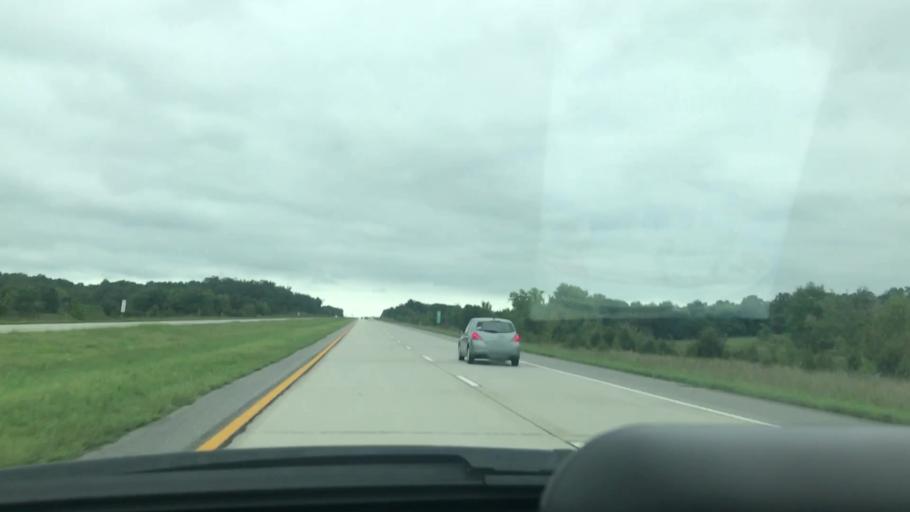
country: US
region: Missouri
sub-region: Greene County
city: Fair Grove
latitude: 37.4674
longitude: -93.1394
